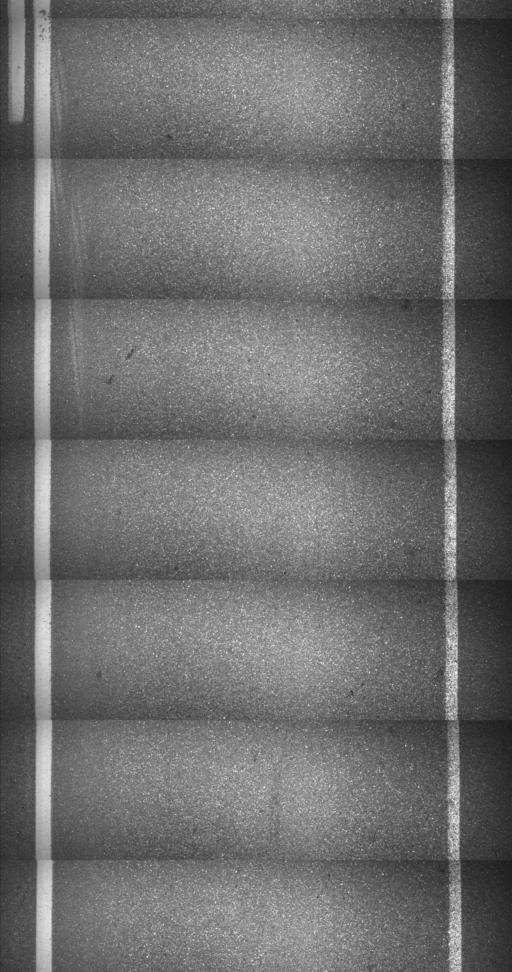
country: US
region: New Hampshire
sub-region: Cheshire County
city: Chesterfield
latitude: 42.9480
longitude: -72.5362
